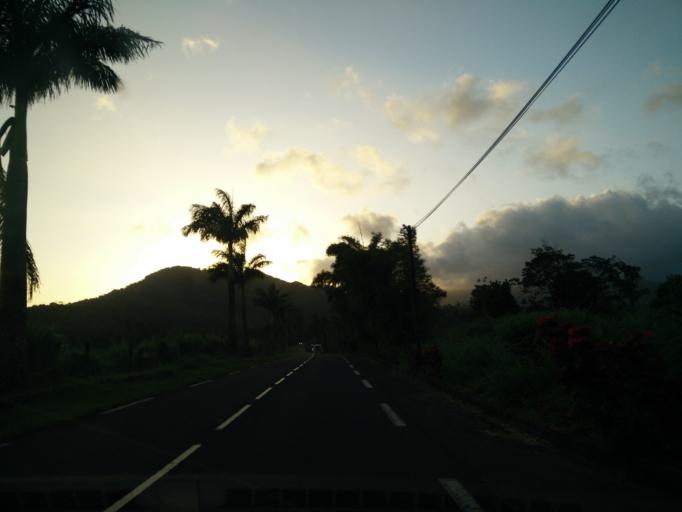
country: MQ
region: Martinique
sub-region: Martinique
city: Le Morne-Rouge
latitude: 14.7613
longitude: -61.1146
